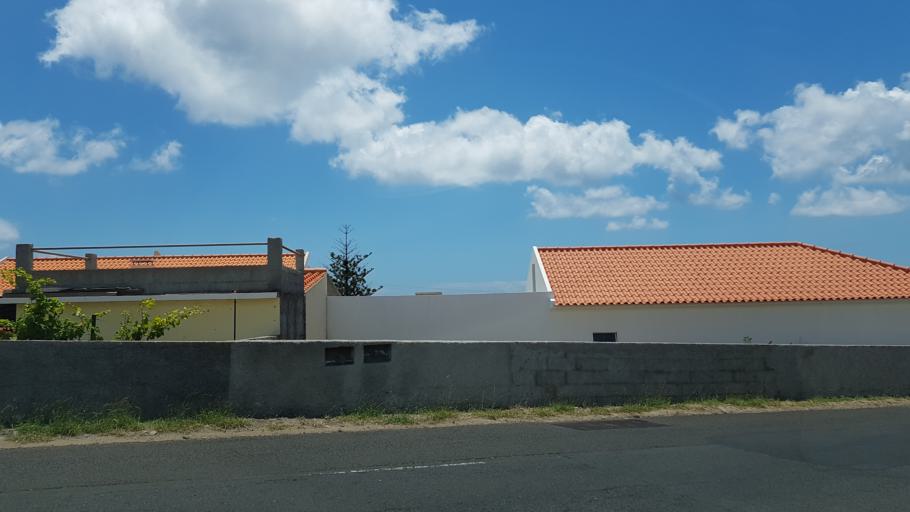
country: PT
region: Madeira
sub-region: Porto Santo
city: Vila de Porto Santo
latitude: 33.0602
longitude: -16.3552
